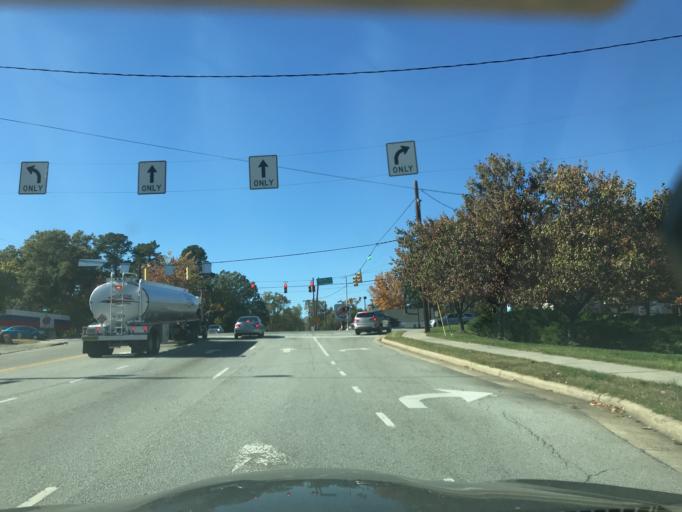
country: US
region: North Carolina
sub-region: Durham County
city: Durham
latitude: 36.0170
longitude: -78.9111
